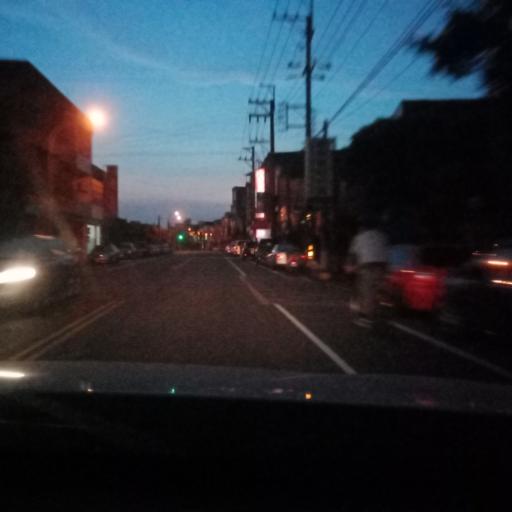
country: TW
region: Taiwan
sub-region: Hsinchu
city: Zhubei
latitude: 24.9013
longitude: 121.0525
